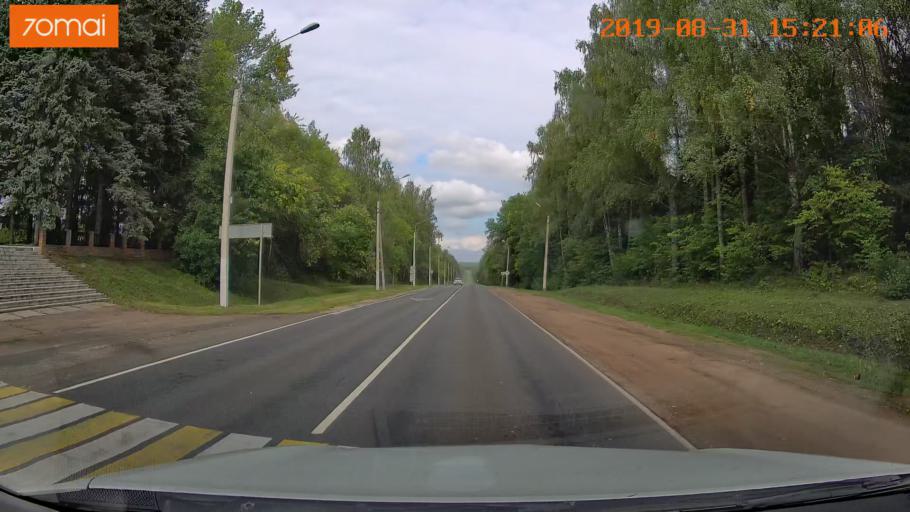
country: RU
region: Kaluga
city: Baryatino
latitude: 54.4940
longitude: 34.4475
